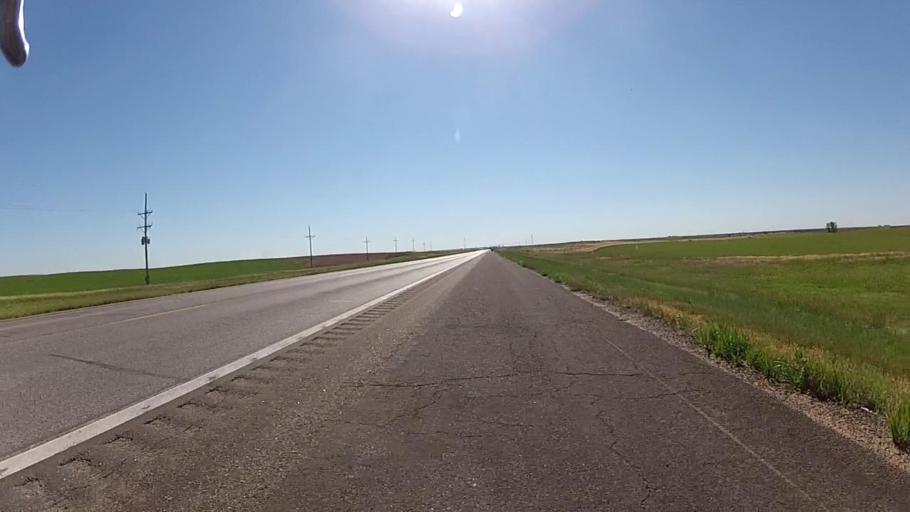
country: US
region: Kansas
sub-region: Kiowa County
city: Greensburg
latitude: 37.5864
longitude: -99.5627
